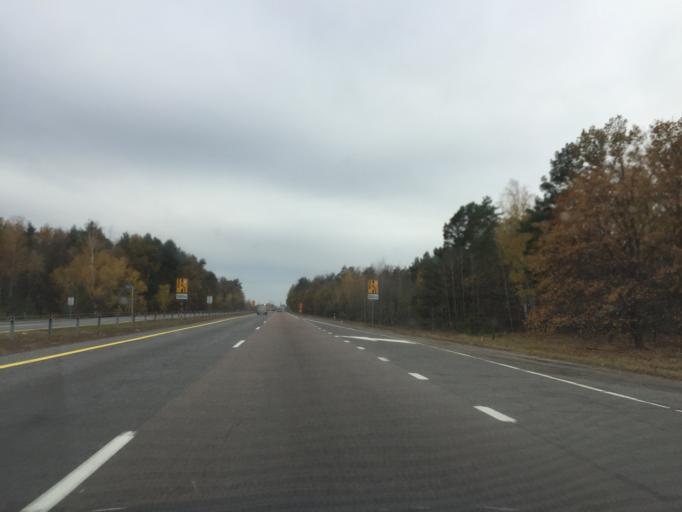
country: BY
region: Gomel
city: Horad Rechytsa
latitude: 52.3316
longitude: 30.5409
